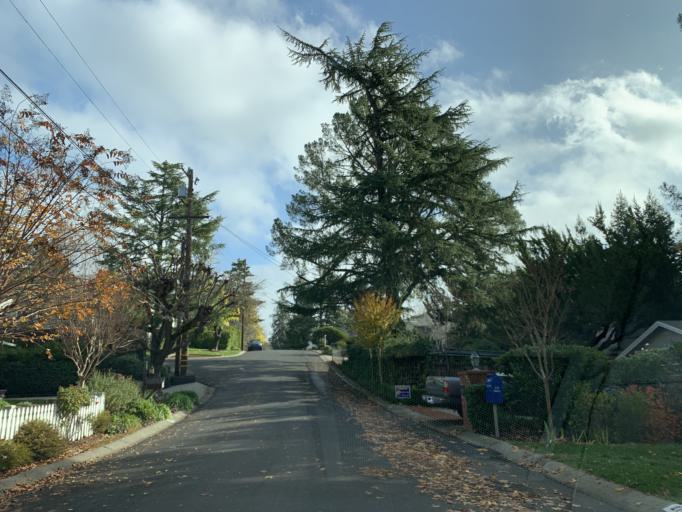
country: US
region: California
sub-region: Contra Costa County
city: Saranap
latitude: 37.8894
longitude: -122.0829
